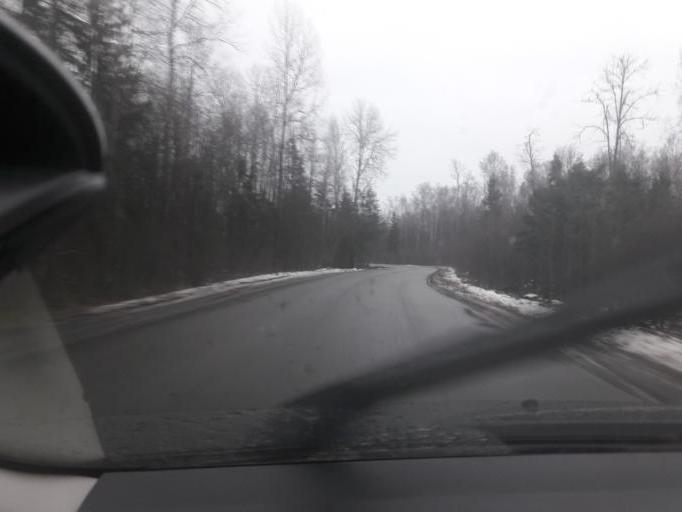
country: RU
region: Moskovskaya
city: Fryazevo
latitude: 55.7641
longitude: 38.5068
